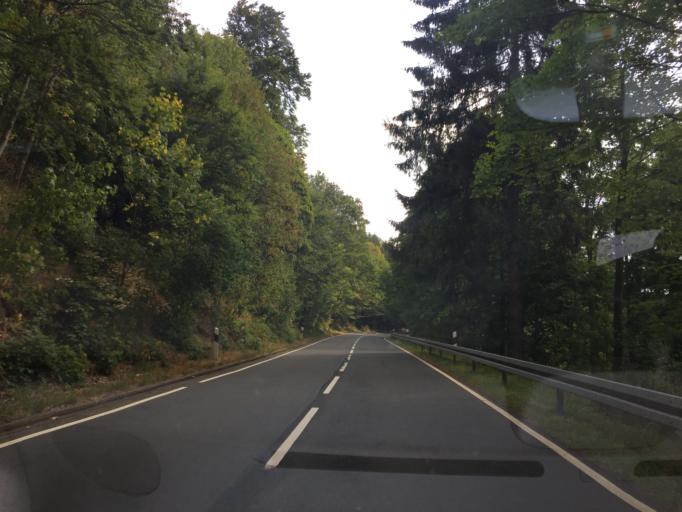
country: DE
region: Lower Saxony
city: Zorge
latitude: 51.6533
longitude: 10.6554
